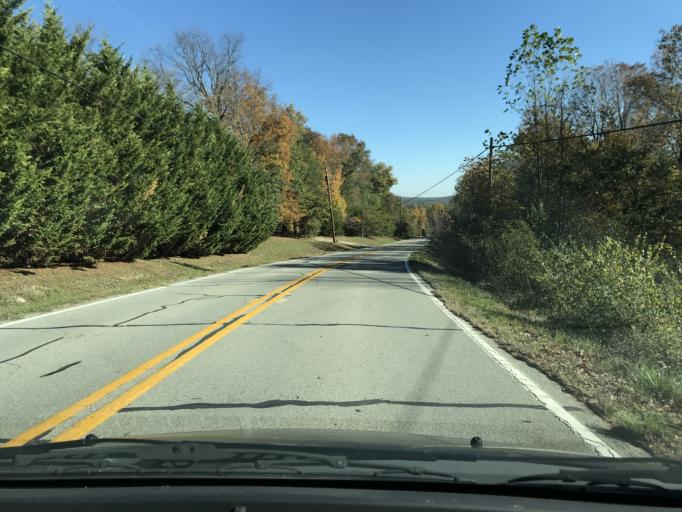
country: US
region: Georgia
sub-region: Dade County
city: Trenton
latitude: 34.8983
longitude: -85.4443
